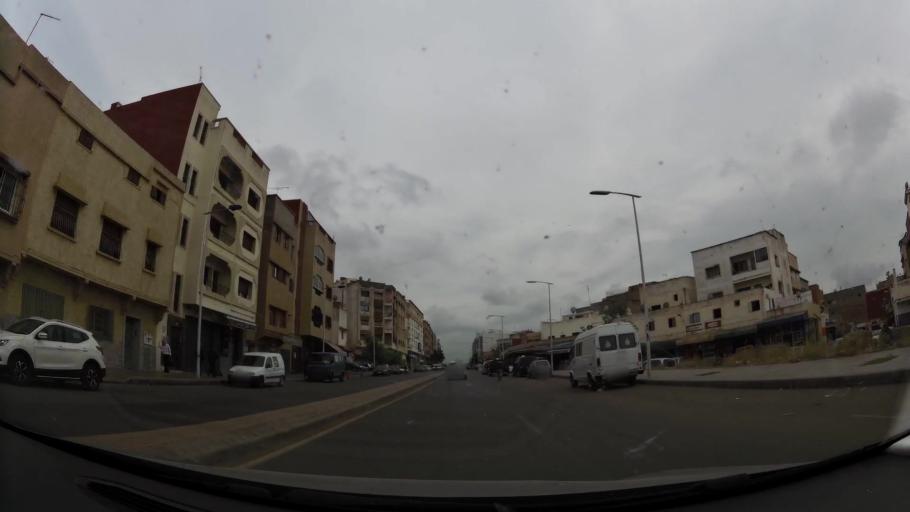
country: MA
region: Rabat-Sale-Zemmour-Zaer
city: Sale
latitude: 34.0396
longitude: -6.8065
